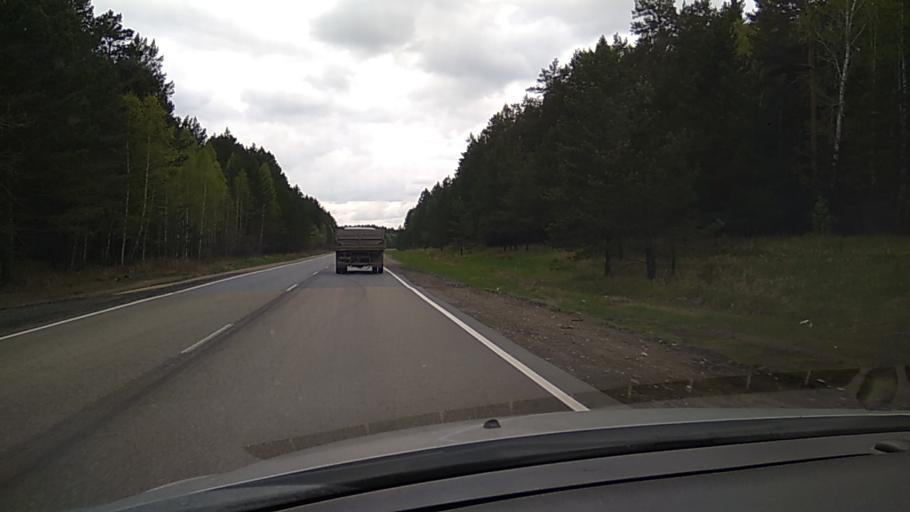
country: RU
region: Kurgan
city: Kataysk
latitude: 56.2993
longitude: 62.3785
